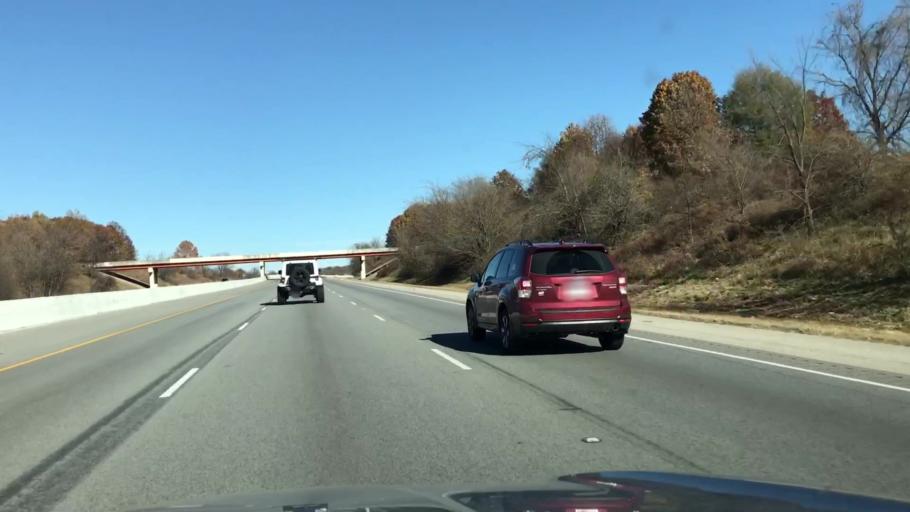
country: US
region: Arkansas
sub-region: Benton County
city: Bethel Heights
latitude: 36.2241
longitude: -94.1794
